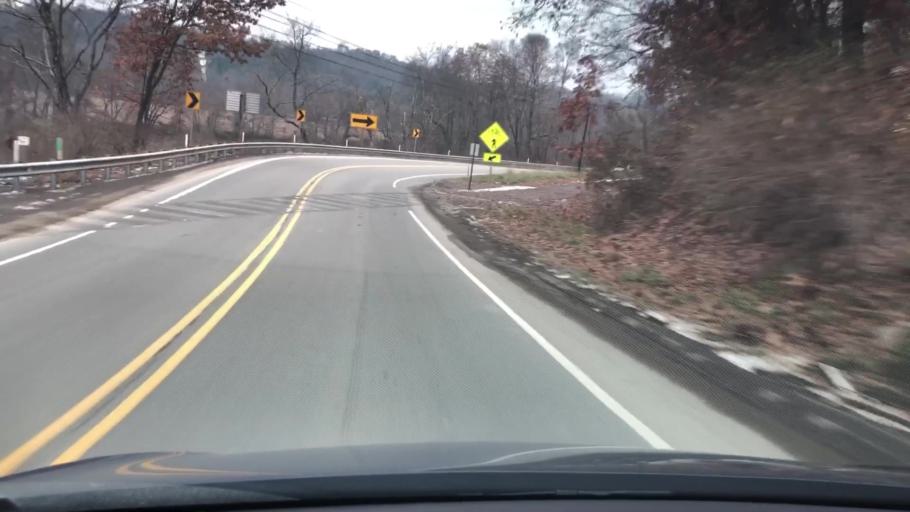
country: US
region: Pennsylvania
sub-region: Clarion County
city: Clarion
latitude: 41.0133
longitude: -79.3045
